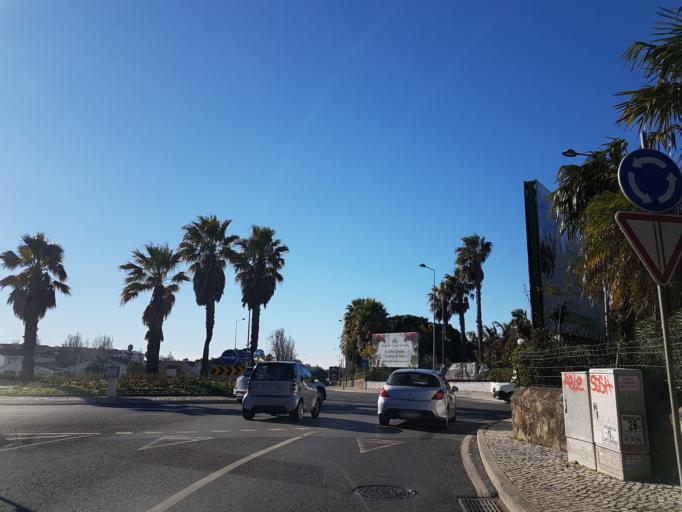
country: PT
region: Lisbon
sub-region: Sintra
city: Sintra
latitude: 38.7736
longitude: -9.3810
